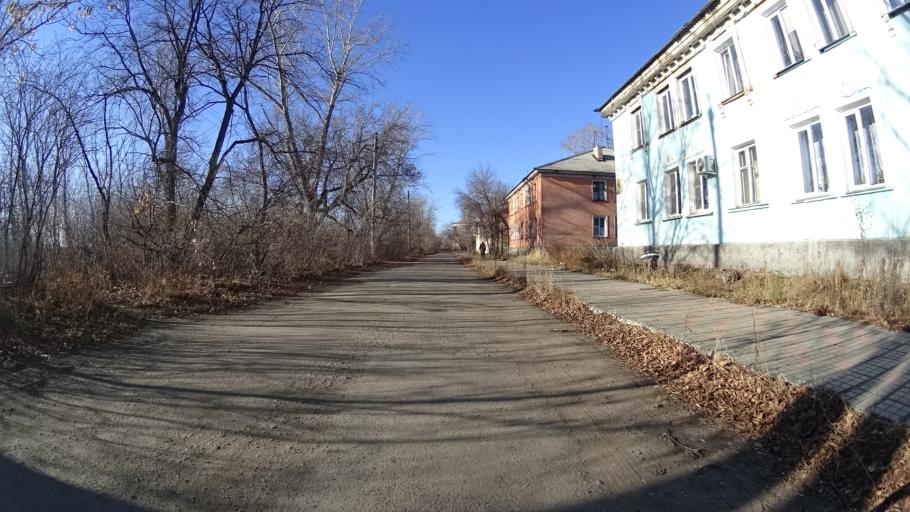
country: RU
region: Chelyabinsk
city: Troitsk
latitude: 54.0428
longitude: 61.6290
